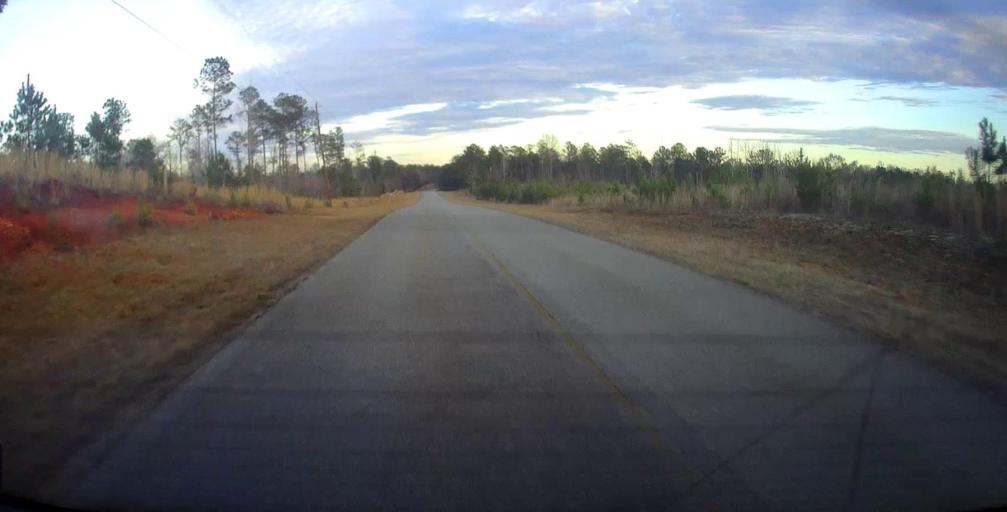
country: US
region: Georgia
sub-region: Harris County
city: Hamilton
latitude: 32.6155
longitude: -84.8304
